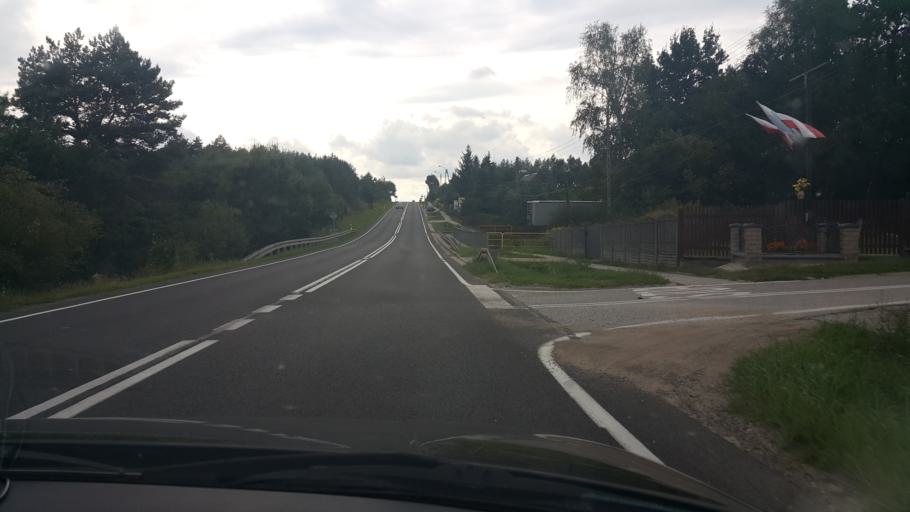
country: PL
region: Swietokrzyskie
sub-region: Powiat skarzyski
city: Blizyn
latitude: 51.0982
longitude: 20.8005
